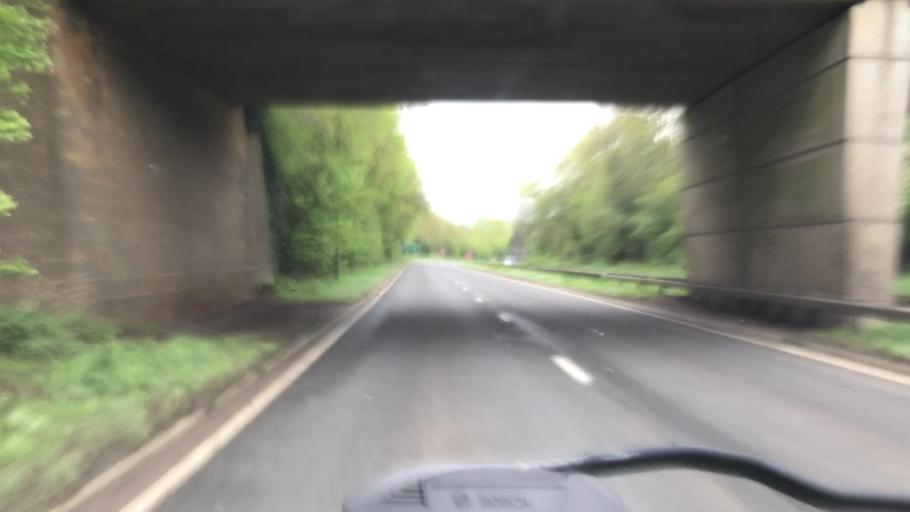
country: GB
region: England
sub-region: Gloucestershire
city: Cirencester
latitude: 51.7141
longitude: -1.9564
